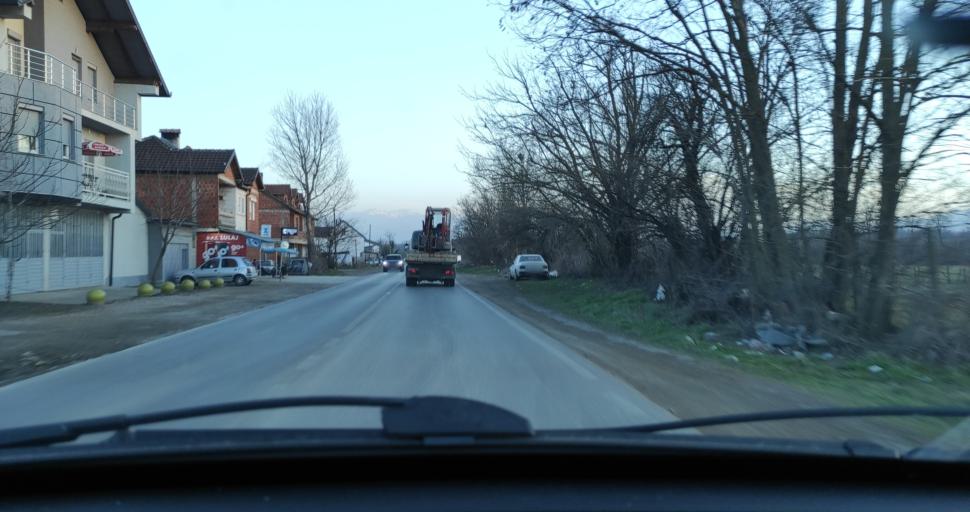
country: XK
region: Gjakova
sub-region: Komuna e Gjakoves
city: Gjakove
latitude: 42.4161
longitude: 20.3989
